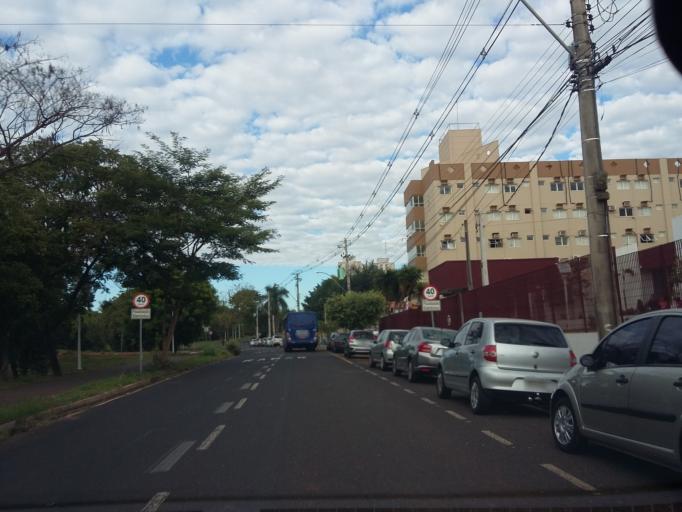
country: BR
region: Sao Paulo
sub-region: Sao Jose Do Rio Preto
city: Sao Jose do Rio Preto
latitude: -20.8320
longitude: -49.4058
